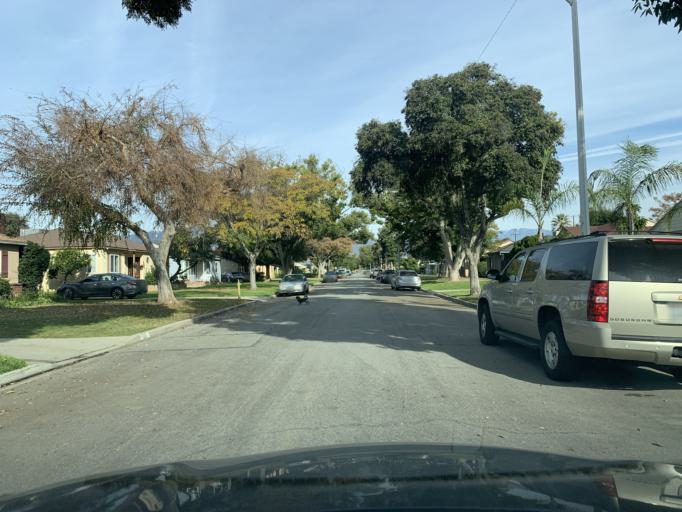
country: US
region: California
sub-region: Los Angeles County
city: West Covina
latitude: 34.0741
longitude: -117.9333
